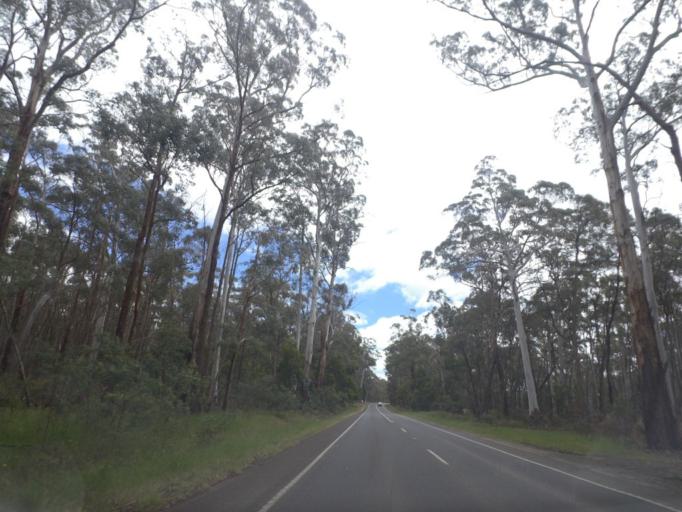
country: AU
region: Victoria
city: Brown Hill
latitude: -37.4718
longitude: 144.1461
